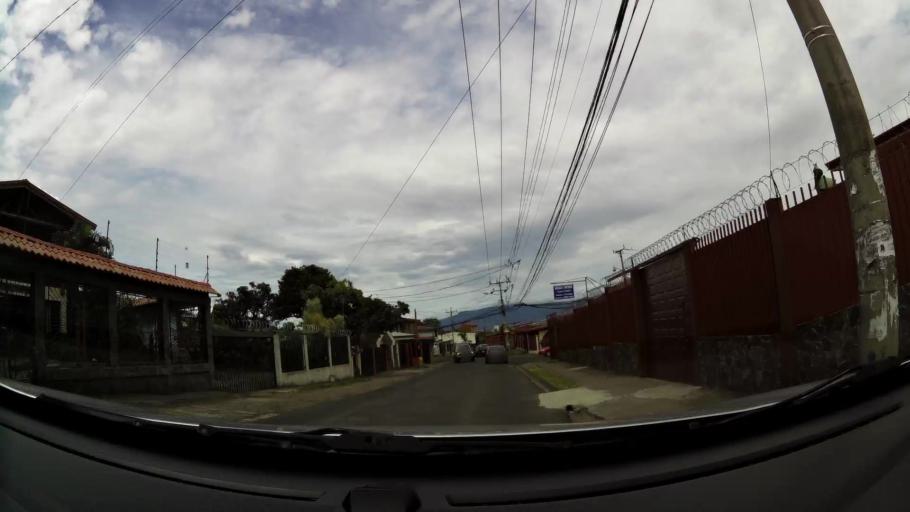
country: CR
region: San Jose
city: San Rafael Arriba
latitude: 9.8936
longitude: -84.0726
